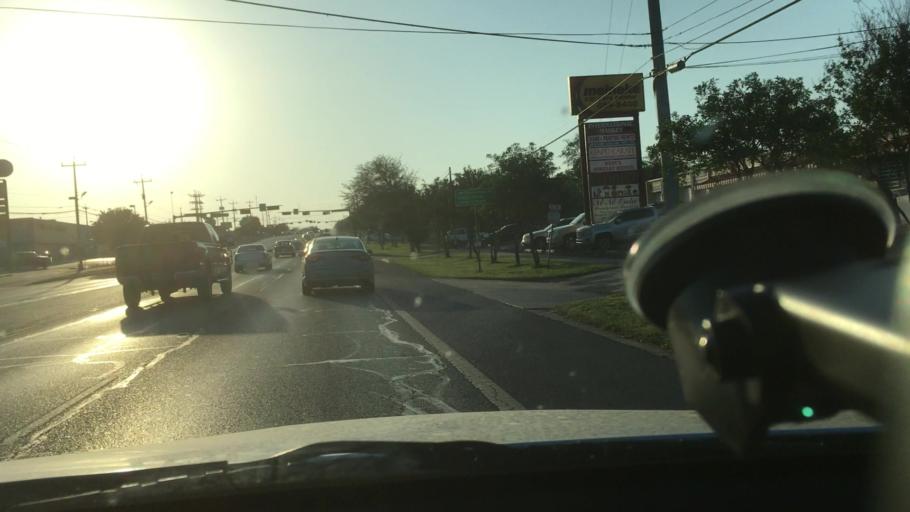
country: US
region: Texas
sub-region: Bexar County
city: Universal City
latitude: 29.5525
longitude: -98.3051
